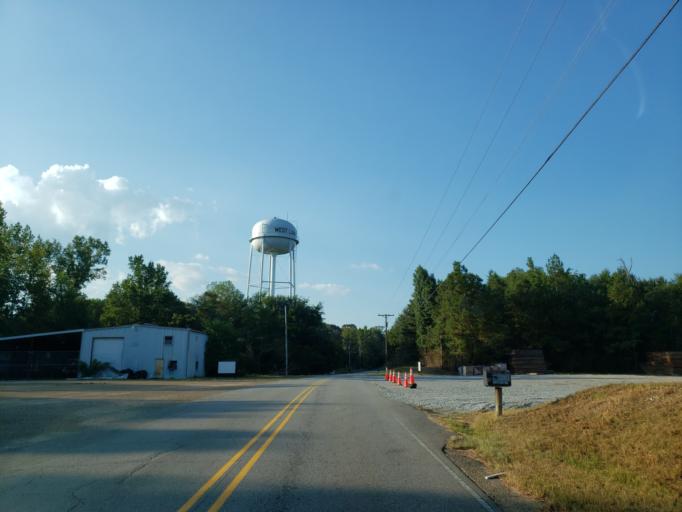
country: US
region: Mississippi
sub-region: Lamar County
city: West Hattiesburg
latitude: 31.3232
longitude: -89.4455
